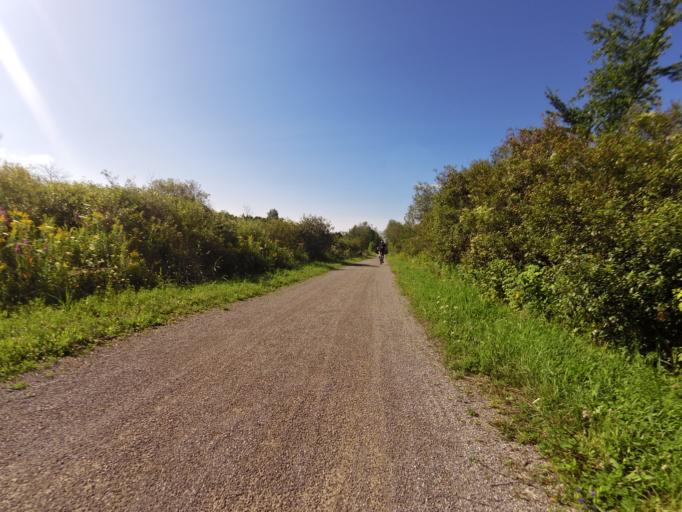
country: CA
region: Ontario
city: Ottawa
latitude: 45.2299
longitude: -75.6193
